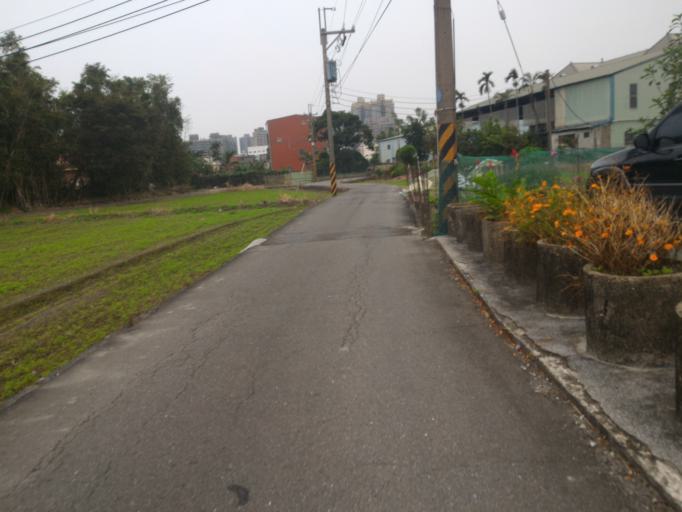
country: TW
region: Taiwan
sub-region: Taoyuan
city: Taoyuan
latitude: 24.9484
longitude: 121.3915
